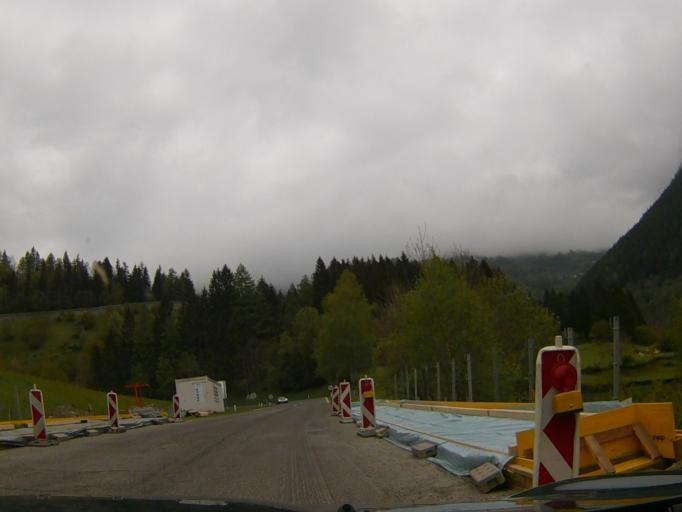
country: AT
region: Carinthia
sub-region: Politischer Bezirk Spittal an der Drau
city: Obervellach
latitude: 46.9644
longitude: 13.1849
